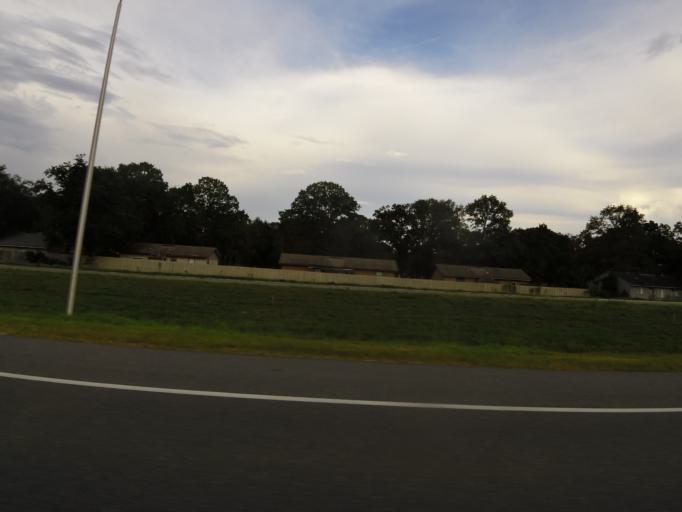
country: US
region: Florida
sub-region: Clay County
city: Lakeside
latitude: 30.1482
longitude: -81.8307
